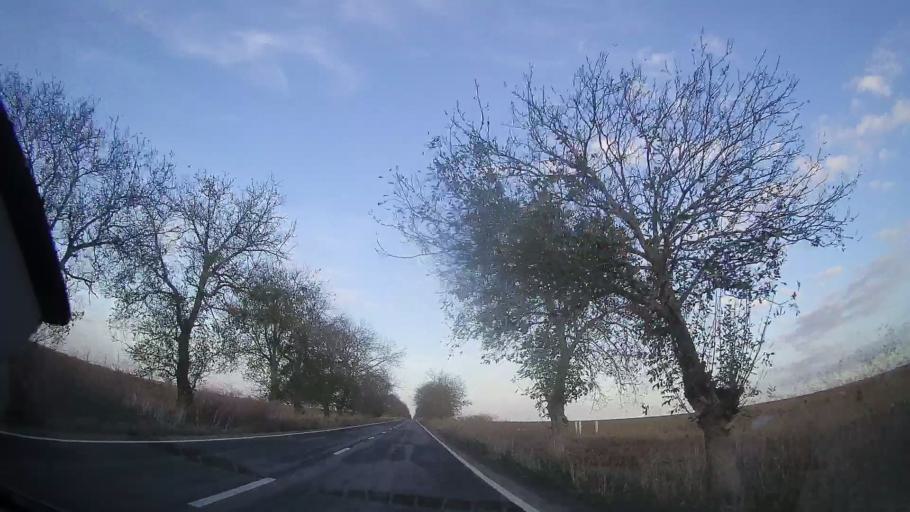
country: RO
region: Constanta
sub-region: Comuna Chirnogeni
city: Chirnogeni
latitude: 43.8594
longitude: 28.2560
